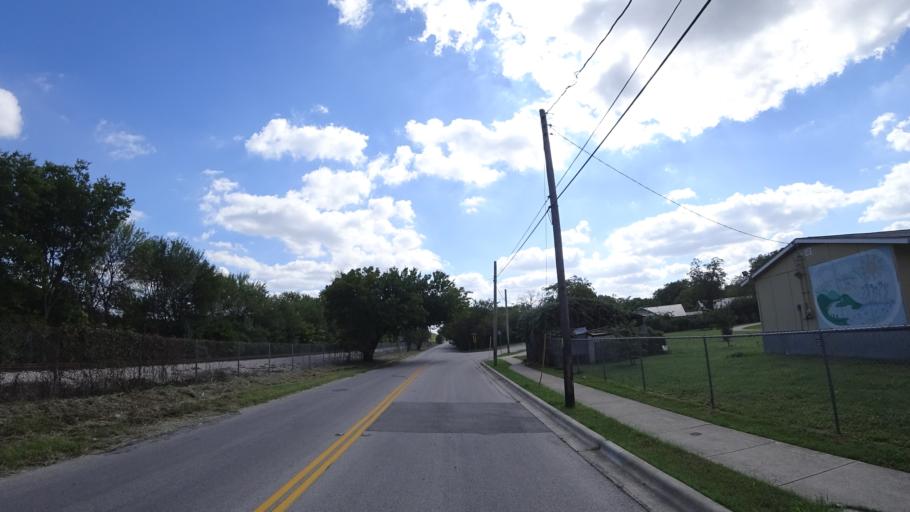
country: US
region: Texas
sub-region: Travis County
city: Austin
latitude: 30.3110
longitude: -97.7159
